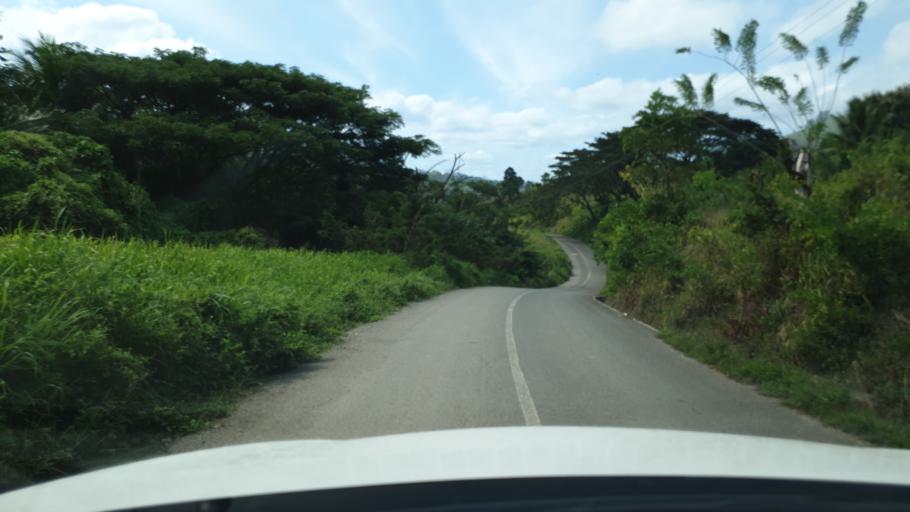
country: PG
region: Central Province
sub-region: Rigo
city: Kwikila
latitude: -9.8330
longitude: 147.5617
